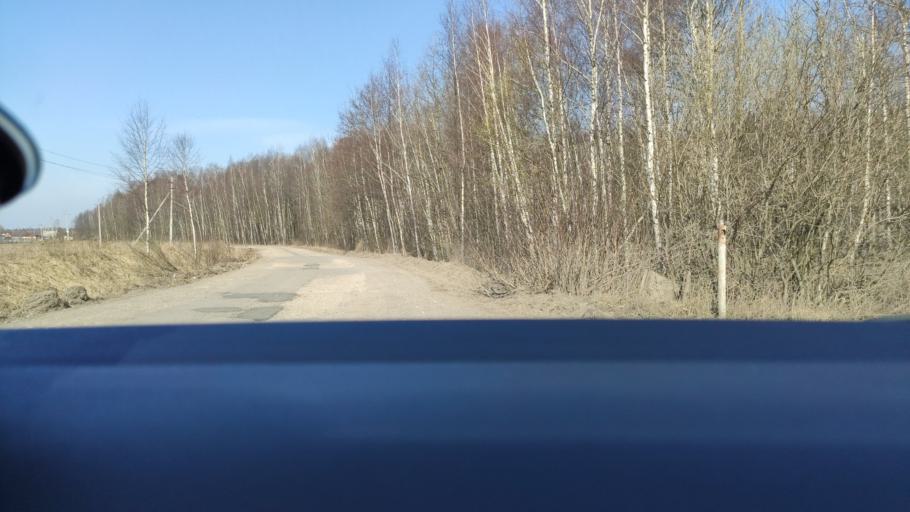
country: RU
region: Moskovskaya
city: Elektrostal'
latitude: 55.7734
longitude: 38.3805
